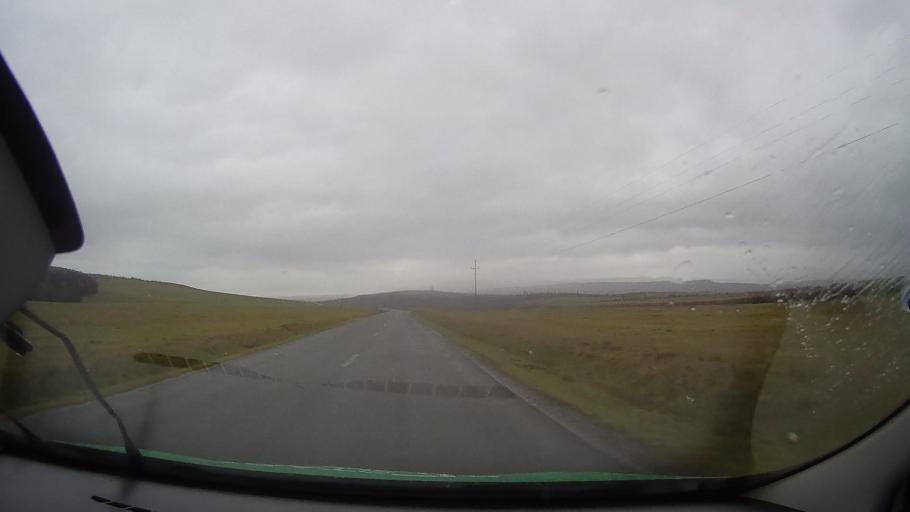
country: RO
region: Mures
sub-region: Comuna Brancovenesti
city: Valenii de Mures
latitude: 46.9055
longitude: 24.7846
